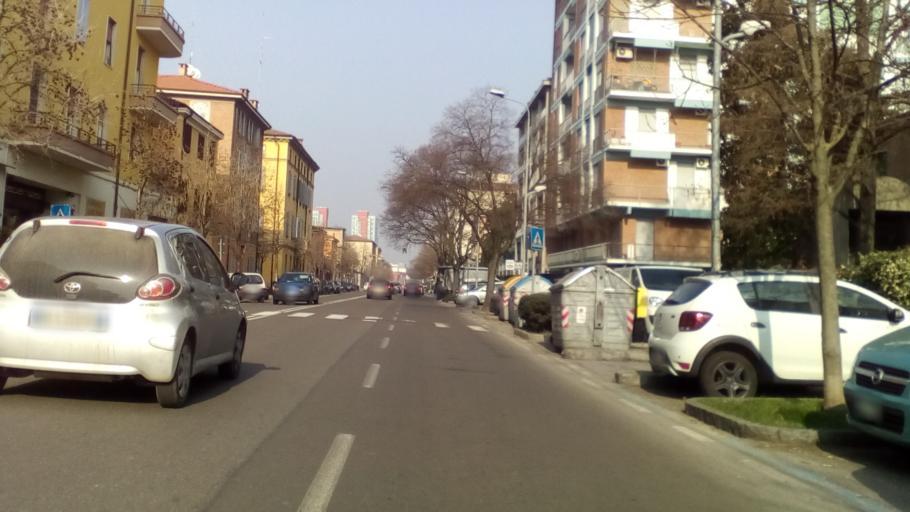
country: IT
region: Emilia-Romagna
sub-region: Provincia di Modena
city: Modena
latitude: 44.6443
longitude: 10.9345
